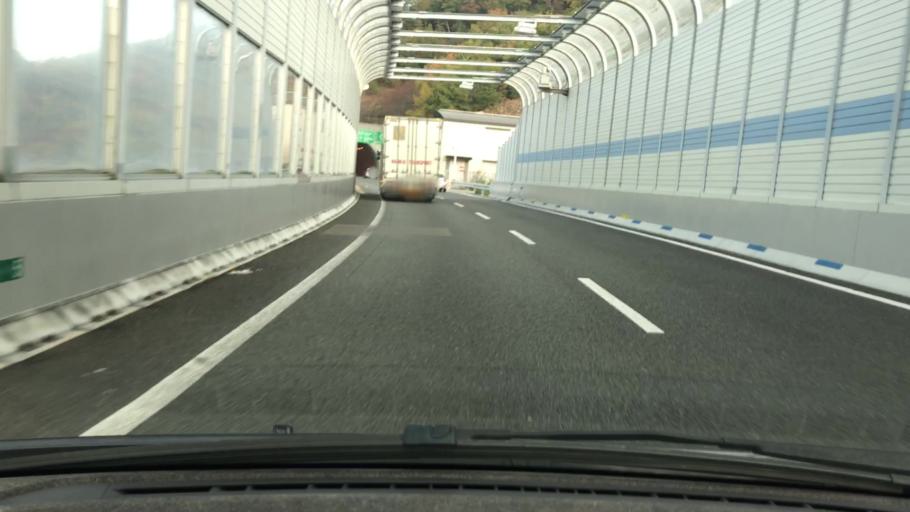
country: JP
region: Hyogo
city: Sandacho
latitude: 34.8232
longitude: 135.2607
